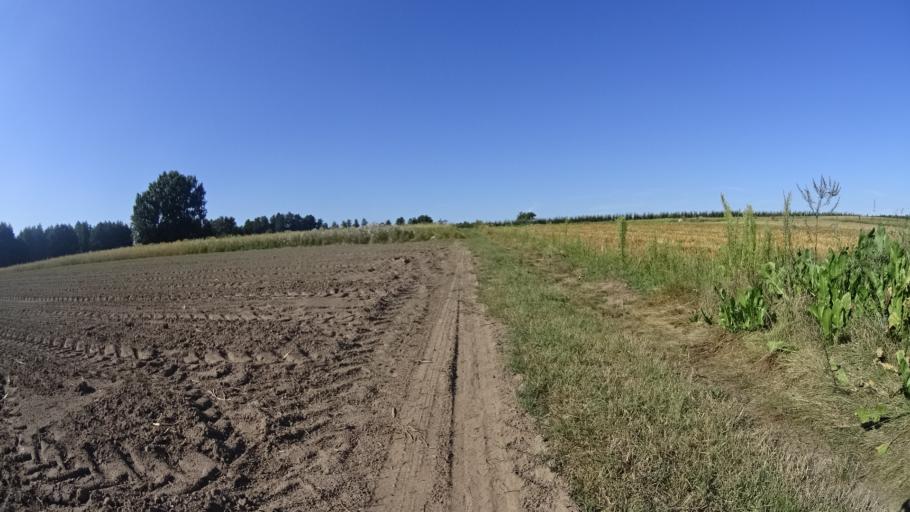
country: PL
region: Masovian Voivodeship
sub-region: Powiat bialobrzeski
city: Wysmierzyce
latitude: 51.6712
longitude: 20.8453
